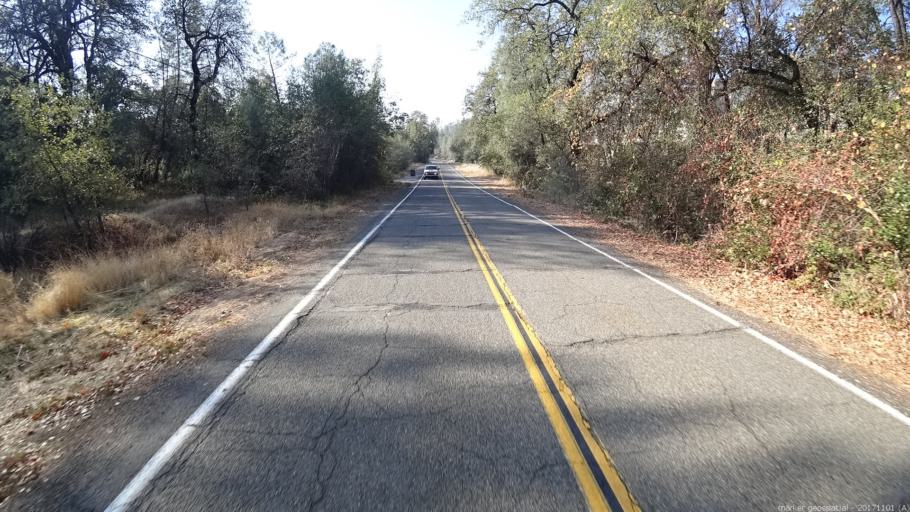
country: US
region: California
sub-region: Shasta County
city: Shasta Lake
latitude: 40.7360
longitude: -122.3196
